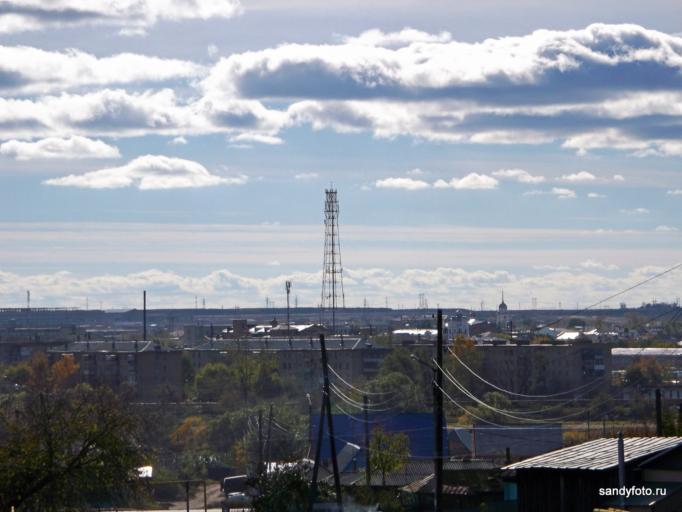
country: RU
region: Chelyabinsk
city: Troitsk
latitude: 54.0990
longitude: 61.5611
